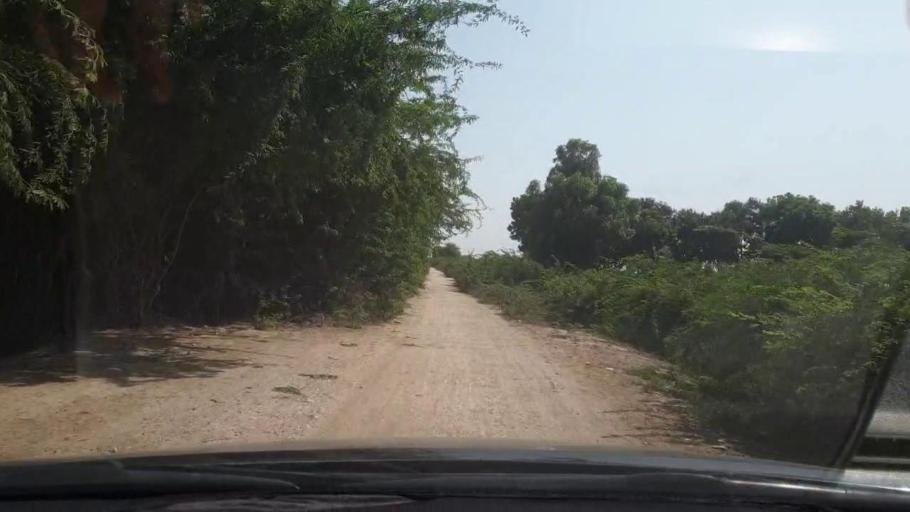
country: PK
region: Sindh
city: Naukot
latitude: 24.8126
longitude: 69.2637
